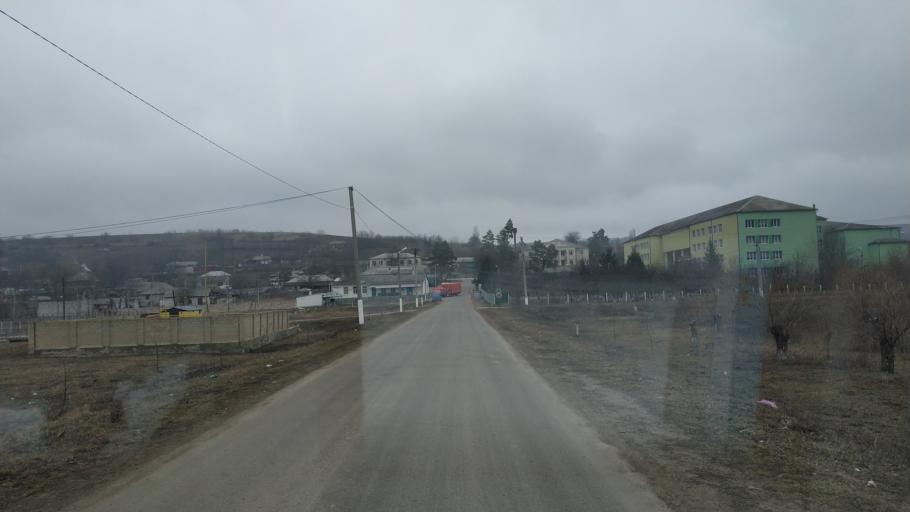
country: MD
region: Hincesti
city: Hincesti
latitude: 46.9789
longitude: 28.4670
